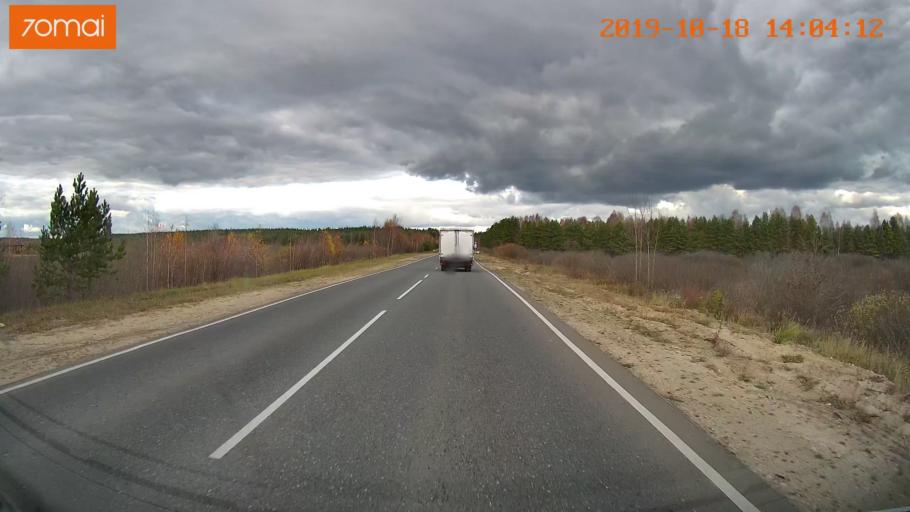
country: RU
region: Rjazan
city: Spas-Klepiki
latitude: 55.1232
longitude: 40.1335
